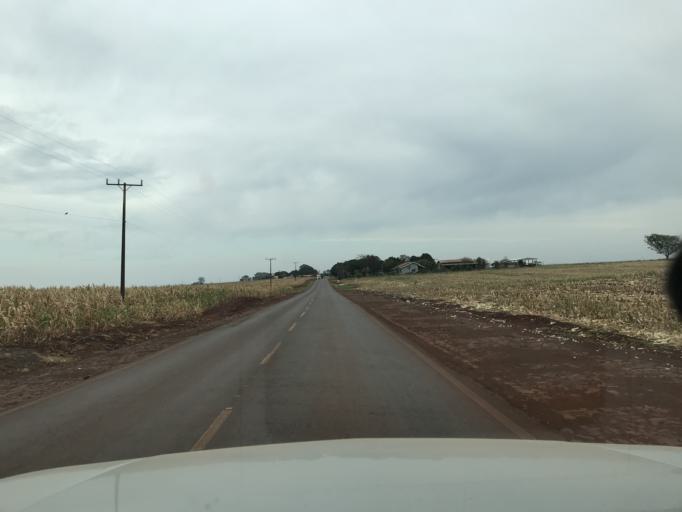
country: BR
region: Parana
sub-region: Palotina
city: Palotina
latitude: -24.4188
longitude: -53.8735
